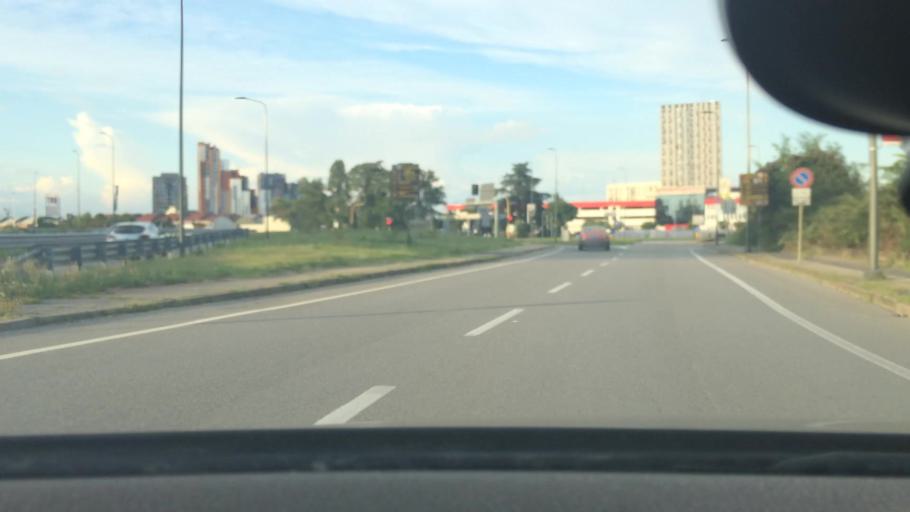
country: IT
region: Lombardy
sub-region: Citta metropolitana di Milano
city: Pero
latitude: 45.5066
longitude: 9.0940
